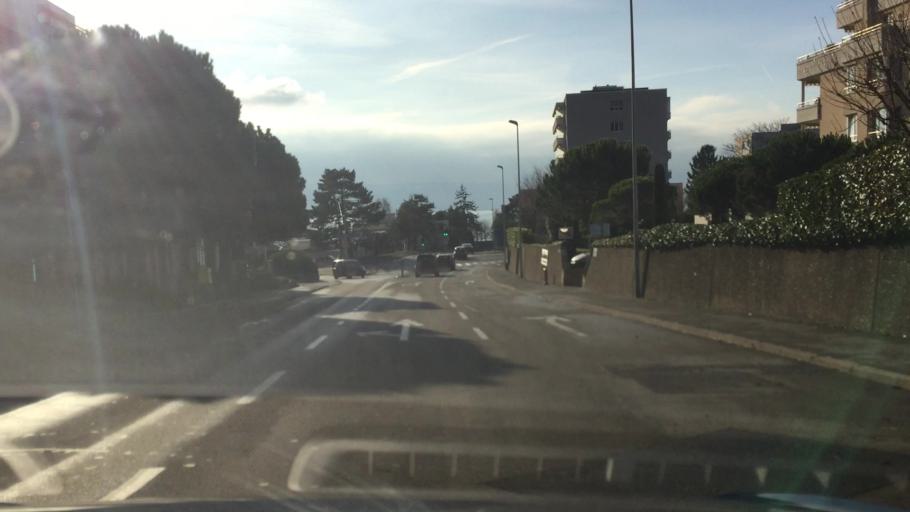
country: CH
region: Vaud
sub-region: Lavaux-Oron District
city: Paudex
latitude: 46.5074
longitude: 6.6693
